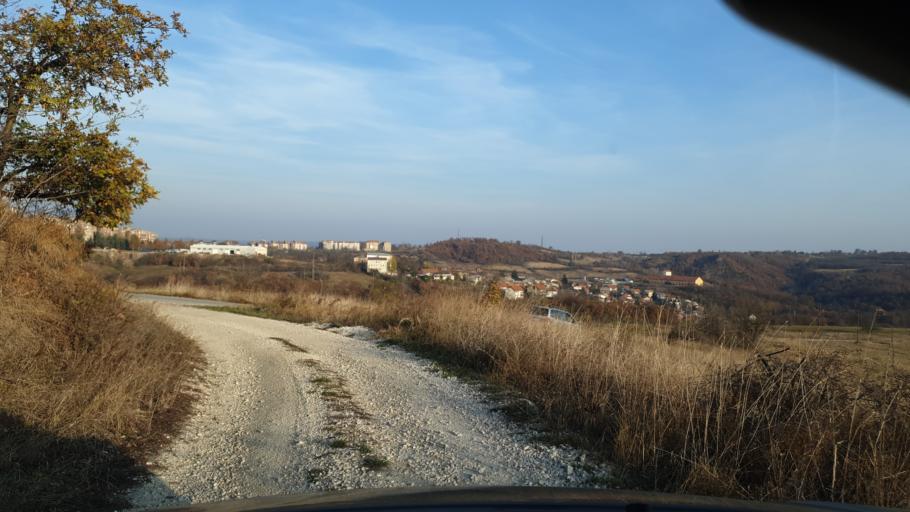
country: RS
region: Central Serbia
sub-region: Borski Okrug
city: Bor
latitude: 44.0513
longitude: 22.0889
